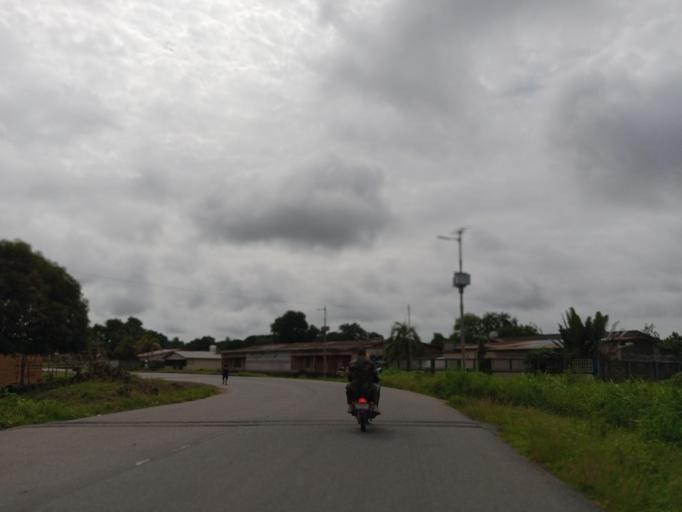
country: SL
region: Northern Province
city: Tintafor
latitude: 8.6237
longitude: -13.2095
